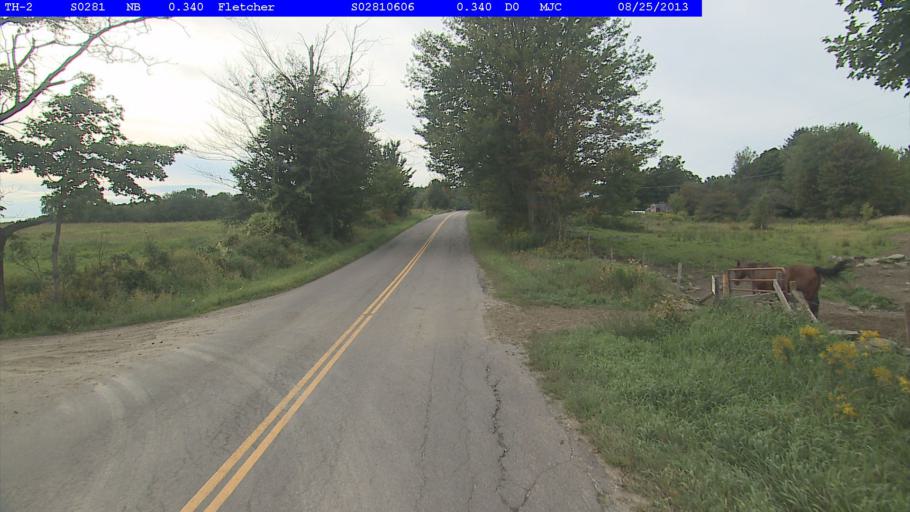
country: US
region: Vermont
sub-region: Chittenden County
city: Milton
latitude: 44.6856
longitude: -72.9204
